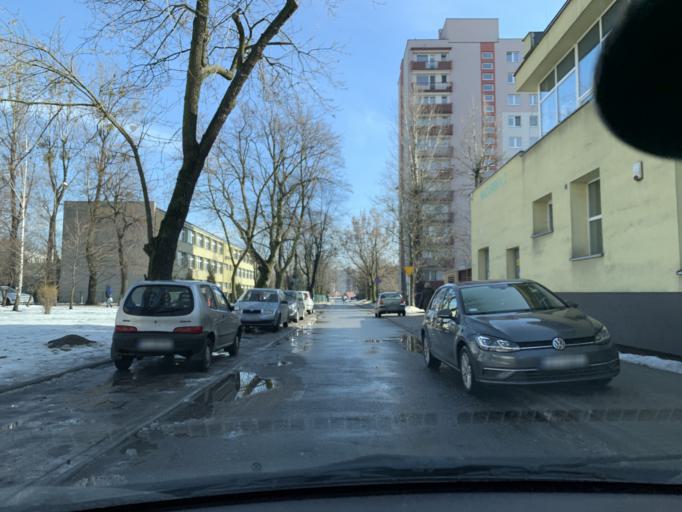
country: PL
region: Silesian Voivodeship
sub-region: Bytom
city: Bytom
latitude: 50.3396
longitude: 18.8922
